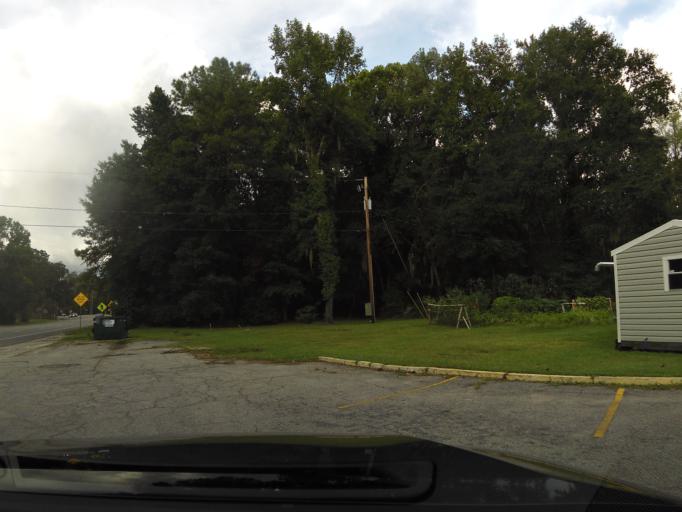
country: US
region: Georgia
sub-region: Liberty County
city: Midway
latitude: 31.8038
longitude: -81.4312
